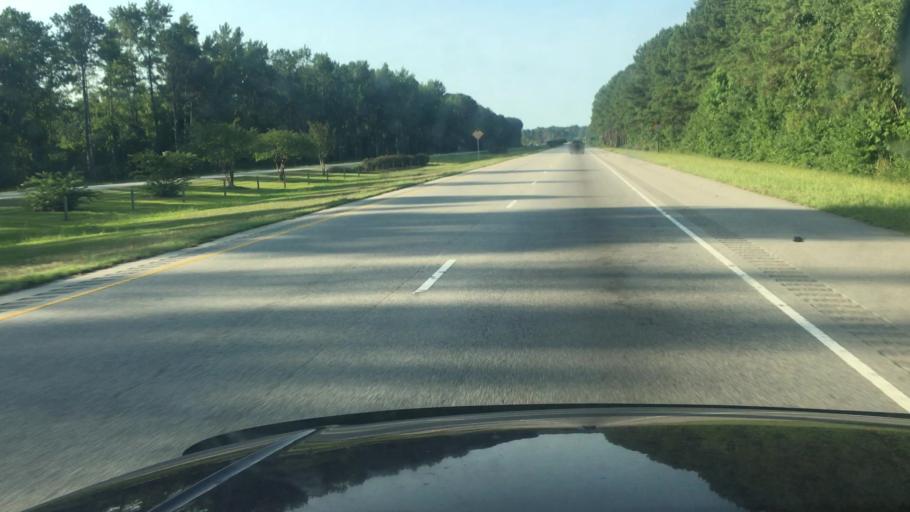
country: US
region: North Carolina
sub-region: Cumberland County
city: Fayetteville
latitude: 34.9920
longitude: -78.8622
